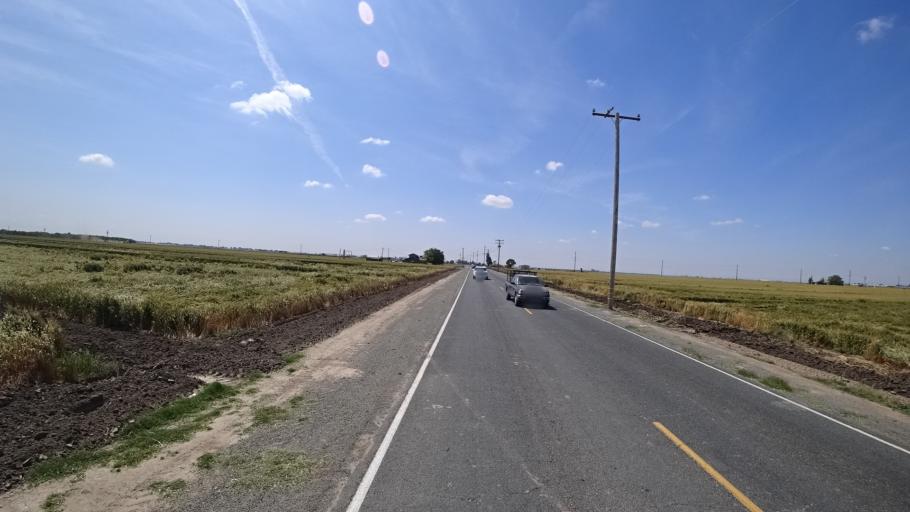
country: US
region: California
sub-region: Tulare County
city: Goshen
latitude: 36.3165
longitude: -119.4932
